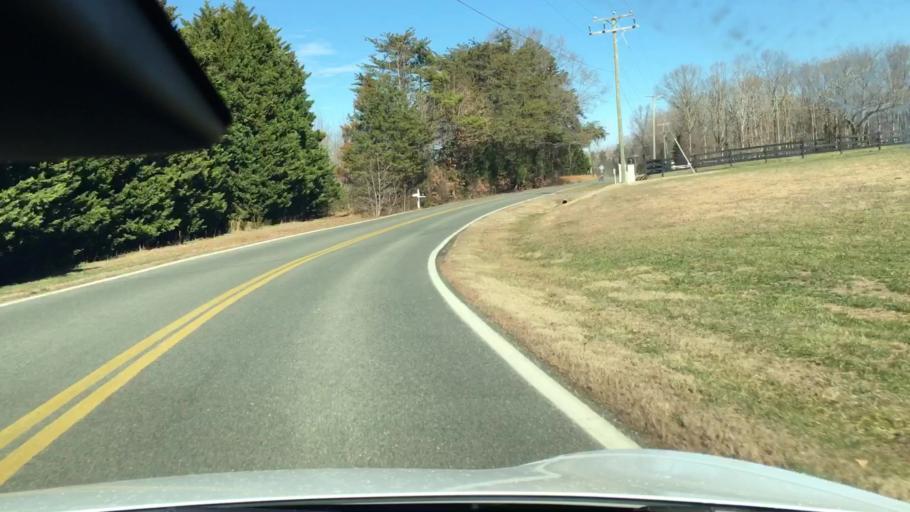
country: US
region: Virginia
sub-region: Powhatan County
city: Powhatan
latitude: 37.5520
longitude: -77.7968
